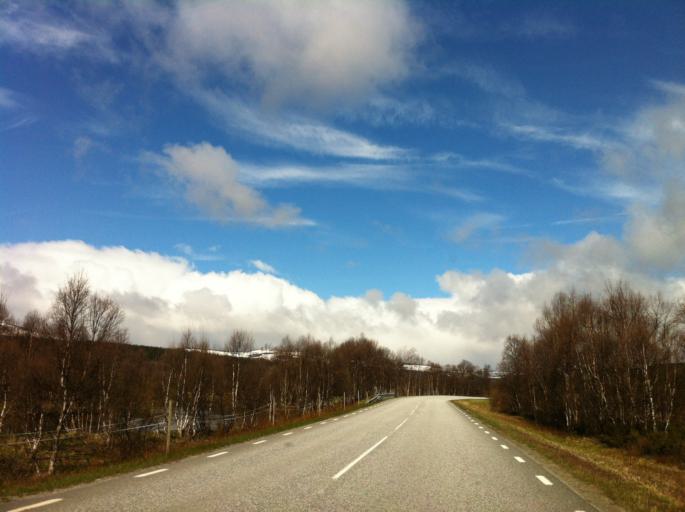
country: SE
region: Jaemtland
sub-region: Are Kommun
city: Are
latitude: 62.5935
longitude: 12.5454
